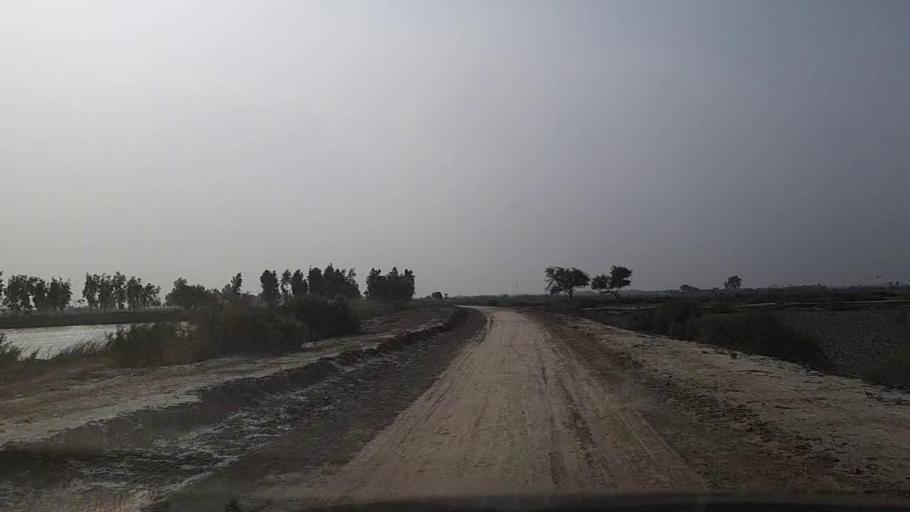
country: PK
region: Sindh
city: Thatta
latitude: 24.7650
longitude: 67.8513
